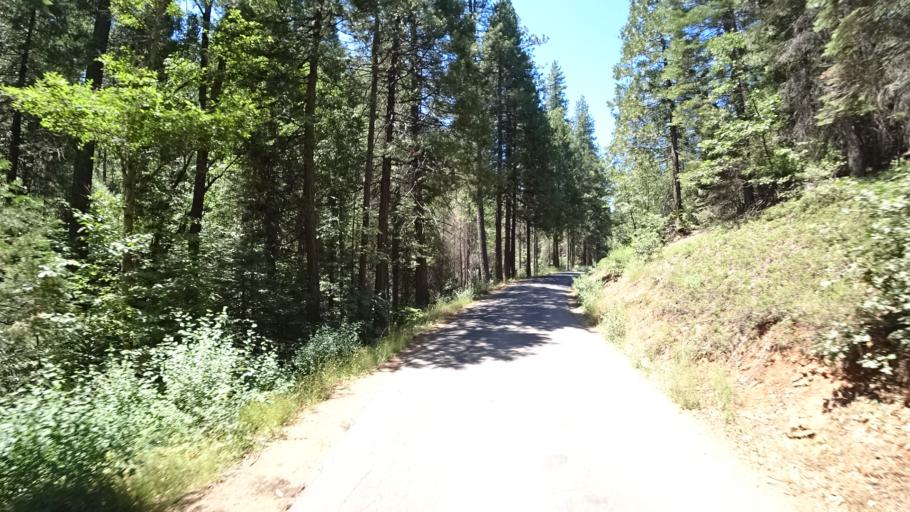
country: US
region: California
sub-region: Calaveras County
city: Arnold
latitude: 38.2211
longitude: -120.3346
